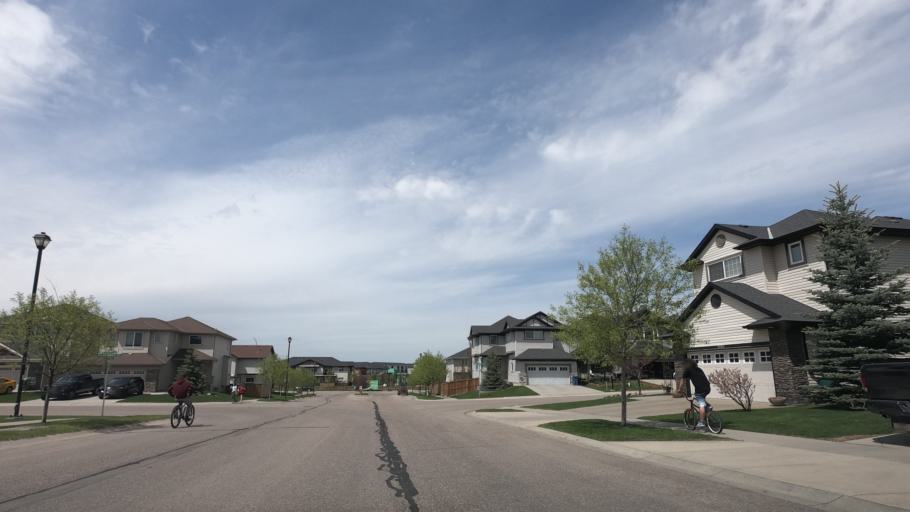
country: CA
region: Alberta
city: Airdrie
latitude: 51.2668
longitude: -114.0291
